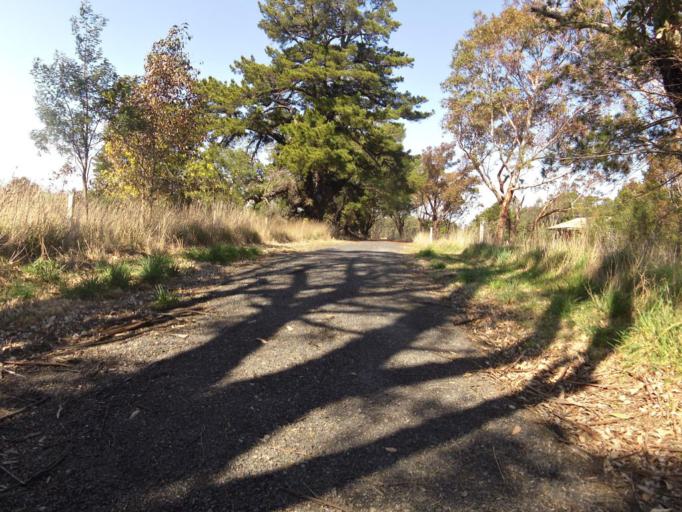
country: AU
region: Victoria
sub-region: Murrindindi
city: Alexandra
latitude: -36.9802
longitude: 145.7172
